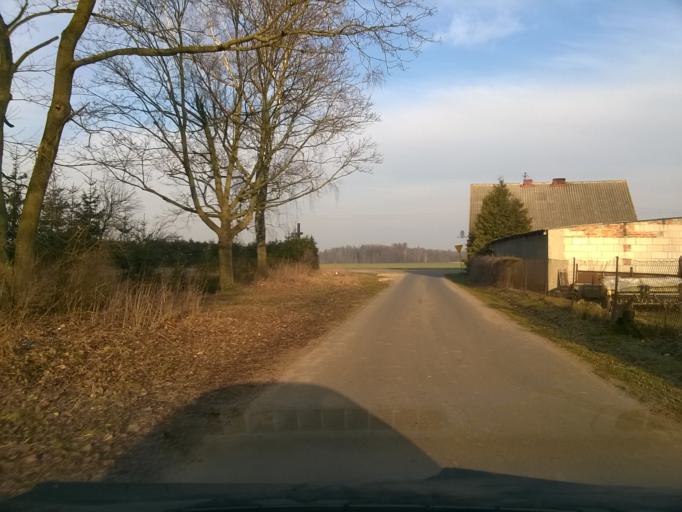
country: PL
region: Kujawsko-Pomorskie
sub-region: Powiat tucholski
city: Kesowo
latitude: 53.5461
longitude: 17.6718
